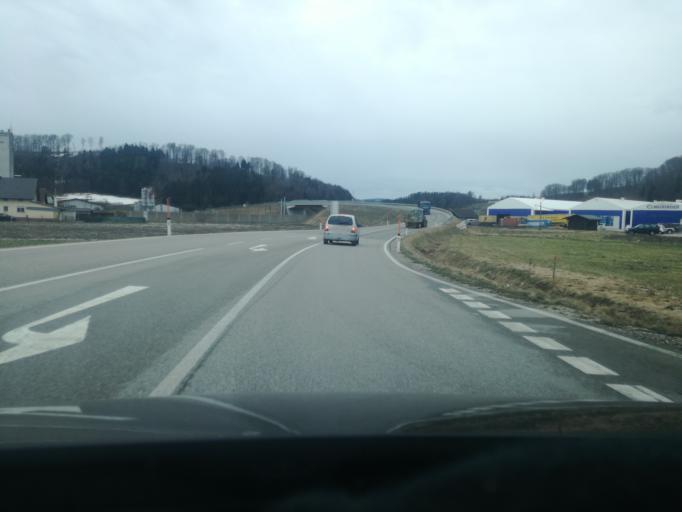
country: AT
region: Upper Austria
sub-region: Politischer Bezirk Vocklabruck
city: Neukirchen an der Vockla
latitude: 48.0291
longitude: 13.5093
